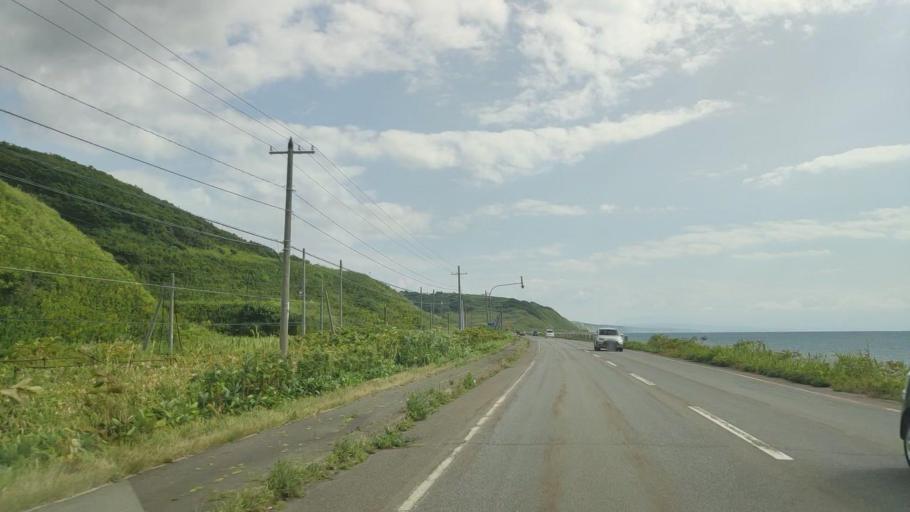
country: JP
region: Hokkaido
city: Rumoi
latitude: 44.1070
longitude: 141.6594
